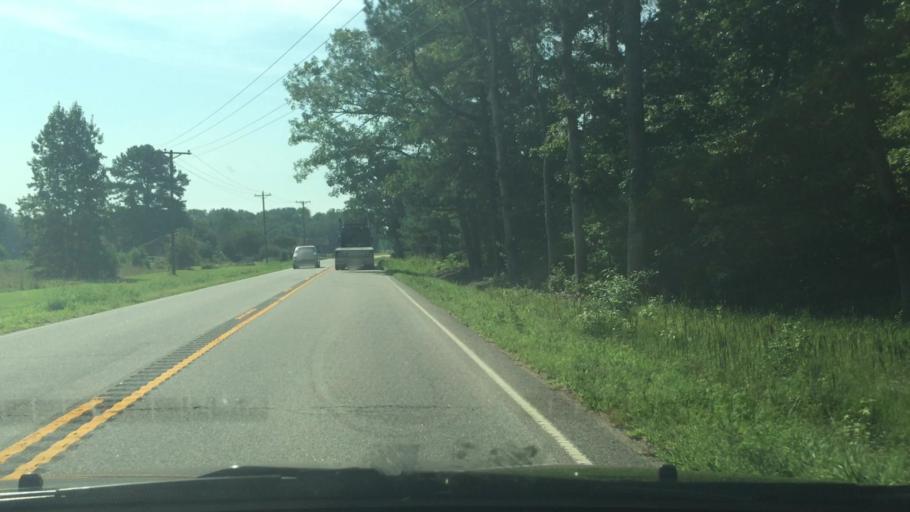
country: US
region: Virginia
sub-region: Sussex County
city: Sussex
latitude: 36.9988
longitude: -77.2628
